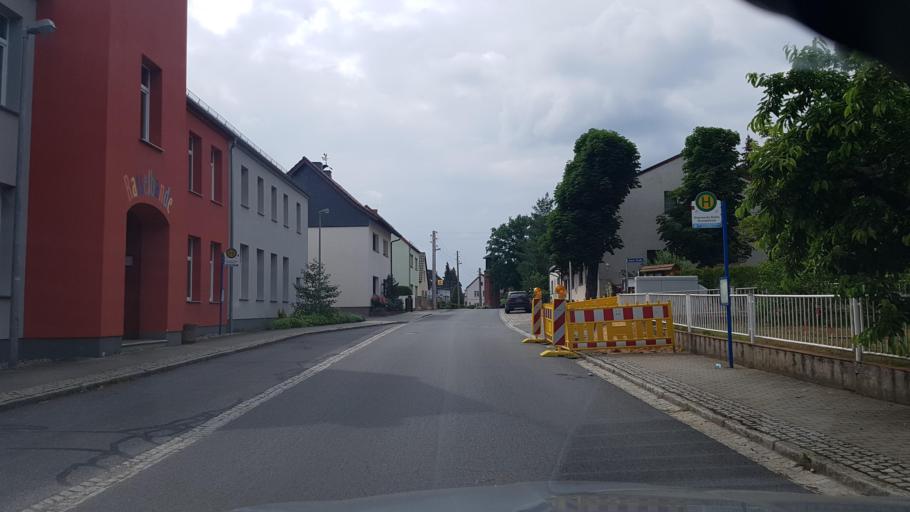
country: DE
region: Brandenburg
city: Elsterwerda
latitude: 51.4712
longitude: 13.5040
